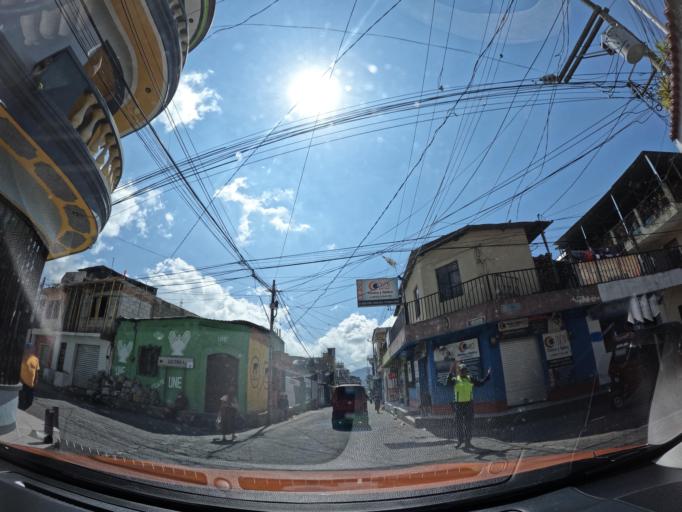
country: GT
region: Solola
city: Santiago Atitlan
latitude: 14.6381
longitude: -91.2312
